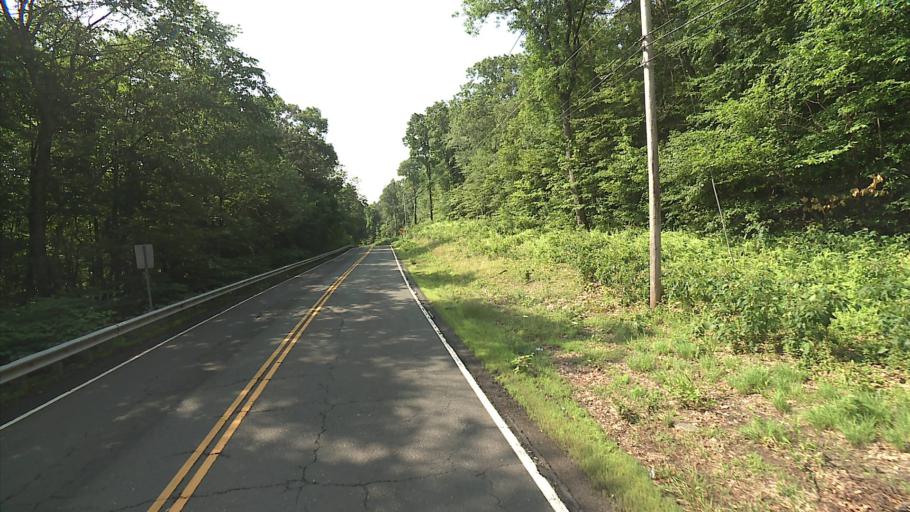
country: US
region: Connecticut
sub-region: New Haven County
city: Wolcott
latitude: 41.5796
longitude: -72.9517
